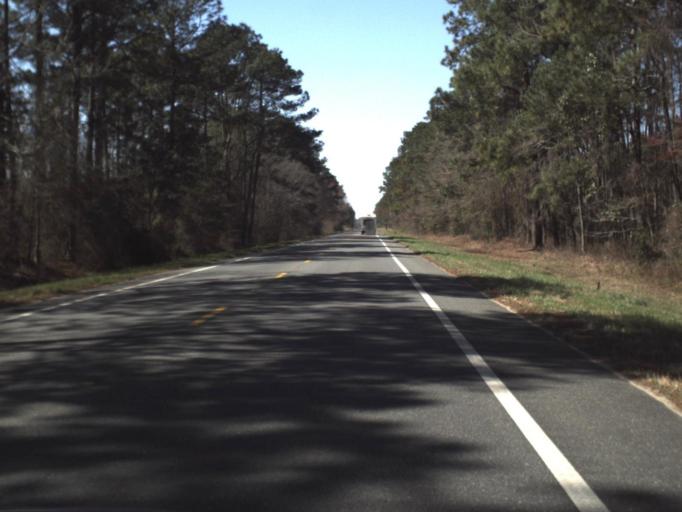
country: US
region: Florida
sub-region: Washington County
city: Chipley
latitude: 30.7907
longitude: -85.3991
